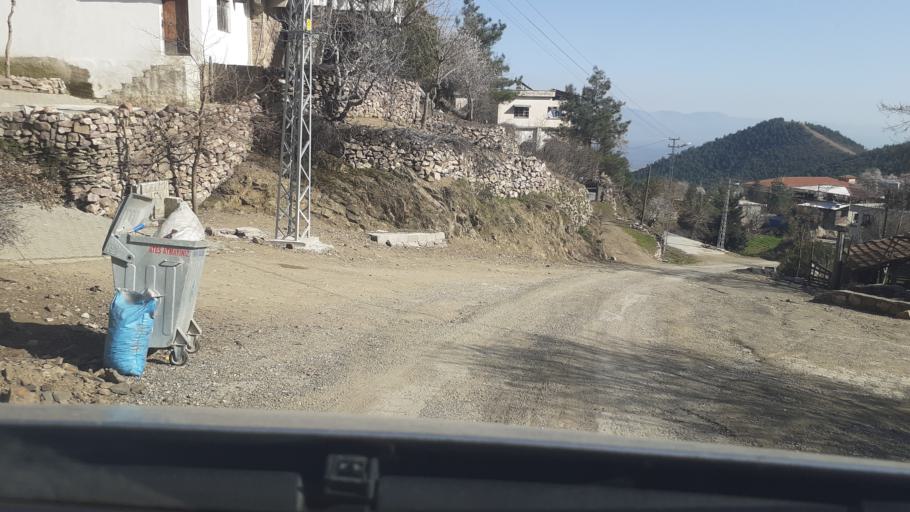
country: TR
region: Hatay
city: Aktepe
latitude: 36.7593
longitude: 36.4512
